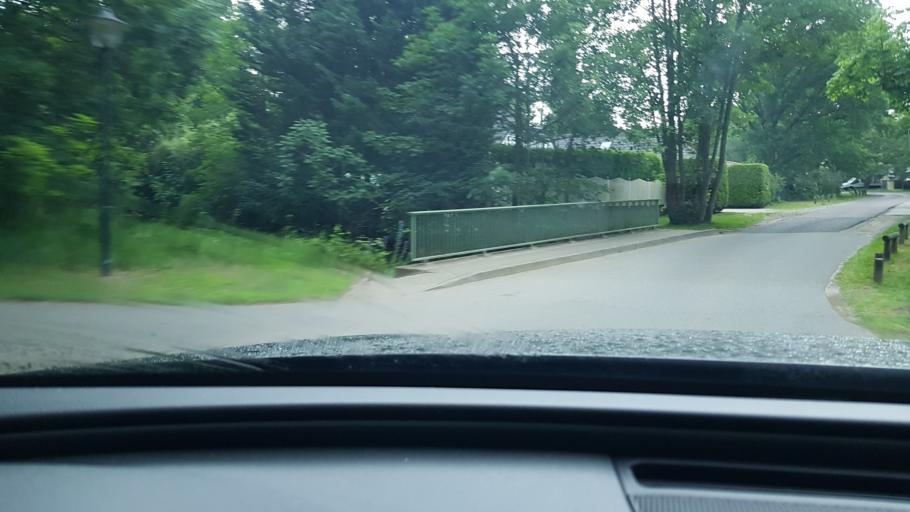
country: DE
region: Berlin
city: Lubars
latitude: 52.6276
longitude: 13.3450
